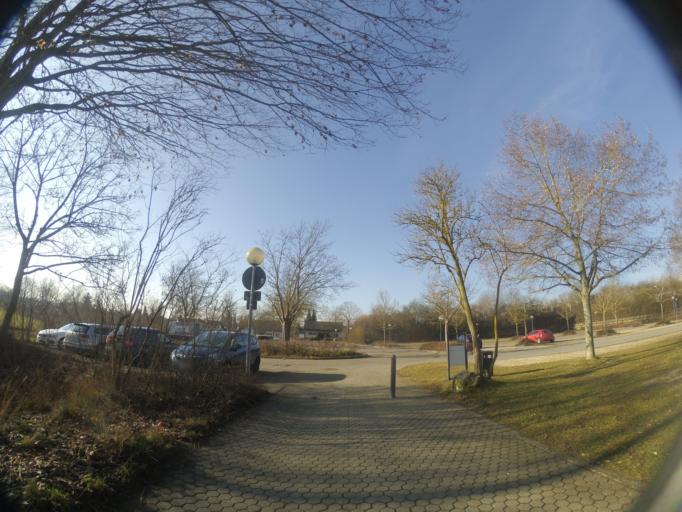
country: DE
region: Baden-Wuerttemberg
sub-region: Tuebingen Region
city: Dornstadt
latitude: 48.4660
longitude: 9.9383
